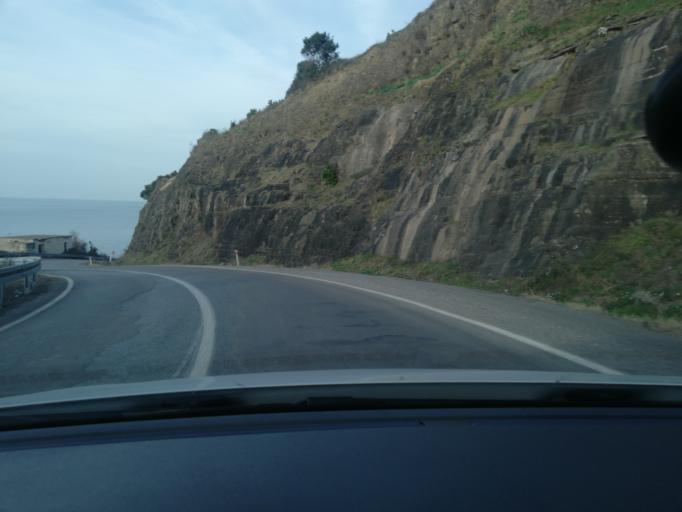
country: TR
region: Zonguldak
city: Tieum
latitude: 41.5525
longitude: 32.0072
